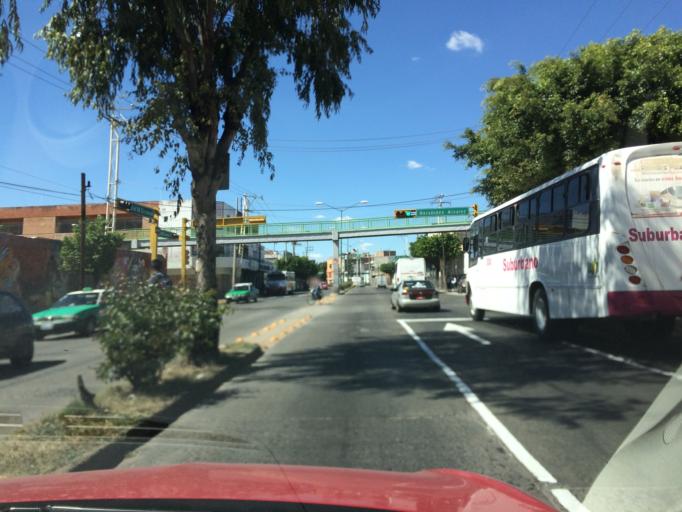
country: MX
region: Guanajuato
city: Leon
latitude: 21.1132
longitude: -101.6777
